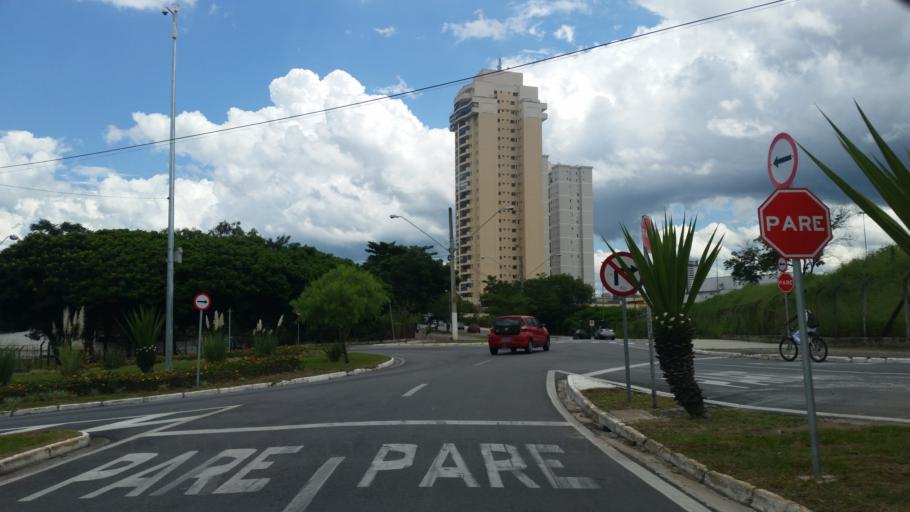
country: BR
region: Sao Paulo
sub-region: Taubate
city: Taubate
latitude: -23.0205
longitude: -45.5813
